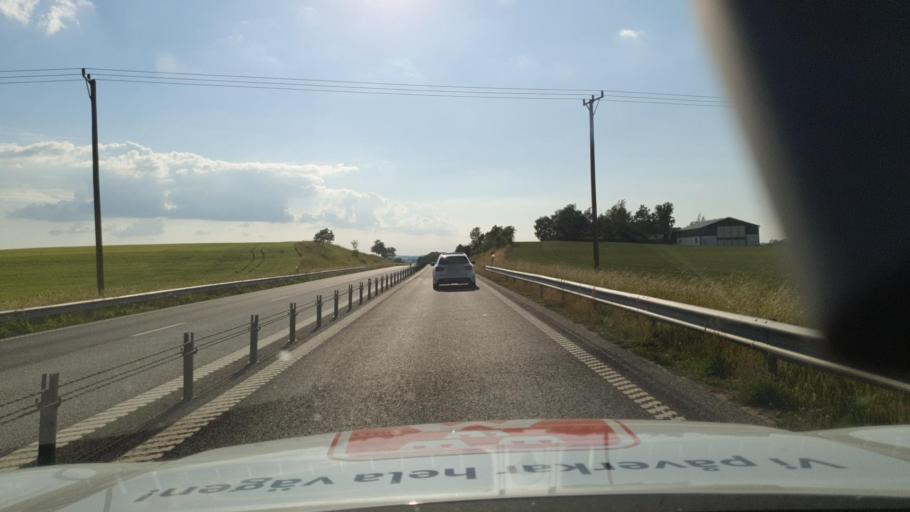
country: SE
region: Skane
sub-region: Skurups Kommun
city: Rydsgard
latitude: 55.4823
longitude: 13.6069
